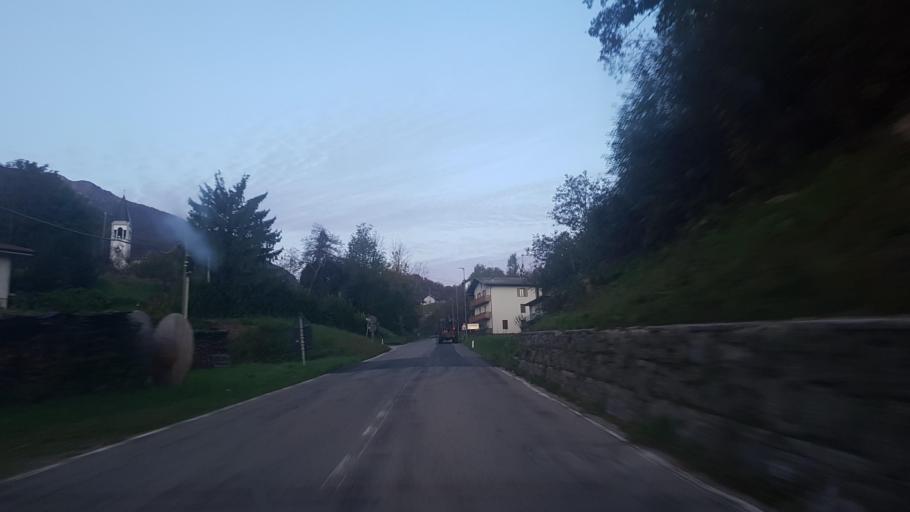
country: IT
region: Friuli Venezia Giulia
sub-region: Provincia di Udine
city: Chiaulis
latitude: 46.3837
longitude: 12.9813
